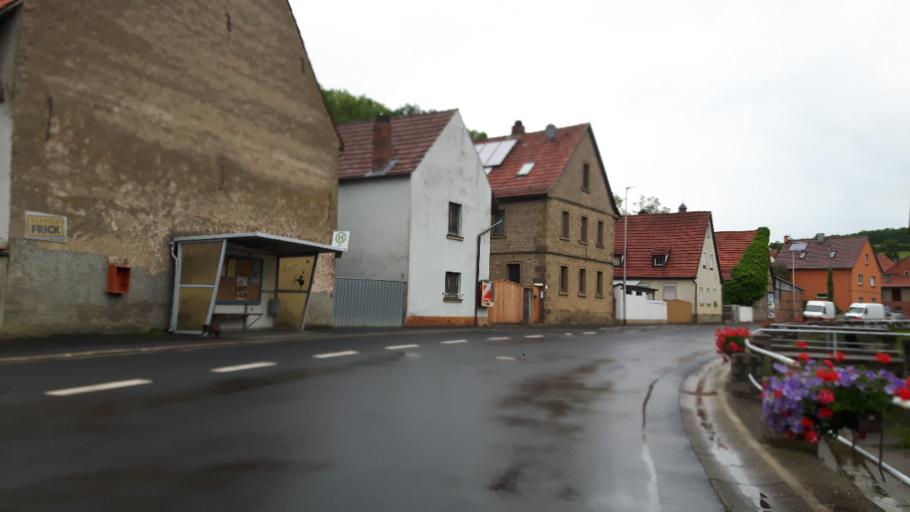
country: DE
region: Bavaria
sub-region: Regierungsbezirk Unterfranken
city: Uchtelhausen
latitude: 50.0939
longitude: 10.2480
